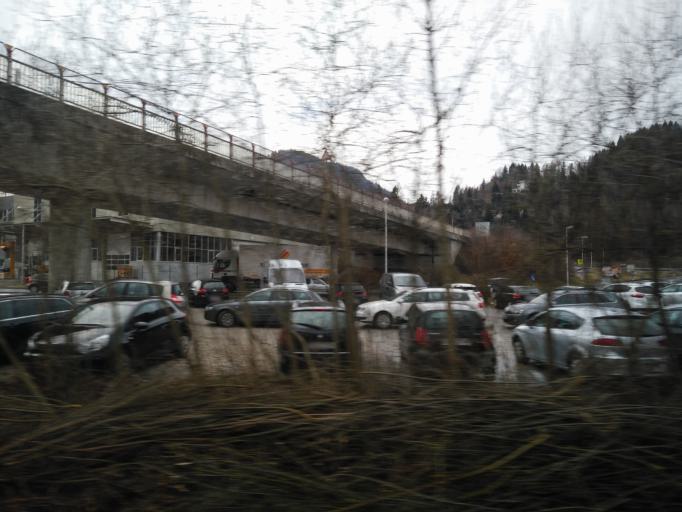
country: AT
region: Salzburg
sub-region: Politischer Bezirk Sankt Johann im Pongau
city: Bischofshofen
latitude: 47.4053
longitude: 13.2202
